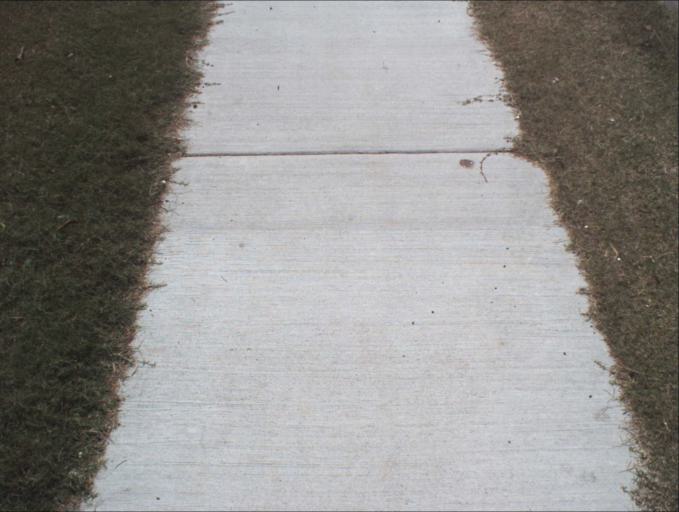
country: AU
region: Queensland
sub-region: Logan
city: Beenleigh
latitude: -27.7024
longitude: 153.2057
